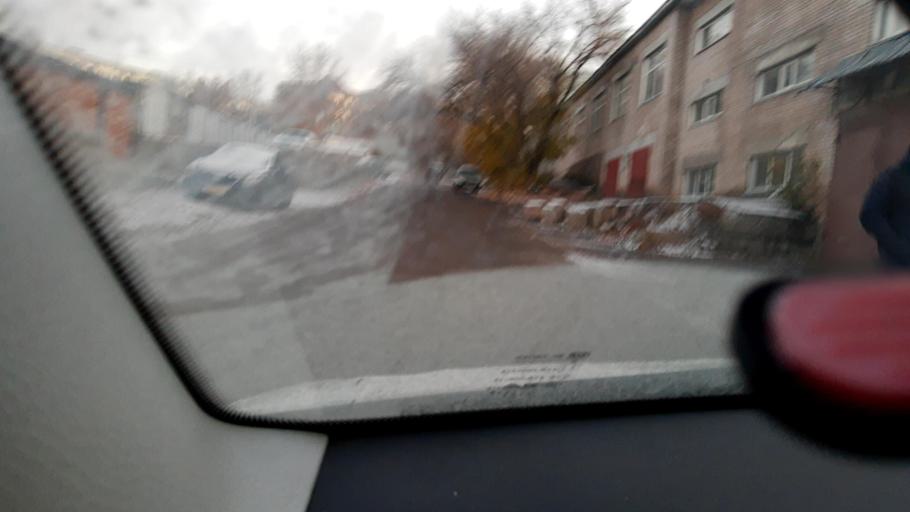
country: RU
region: Bashkortostan
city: Ufa
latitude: 54.7251
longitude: 55.9799
